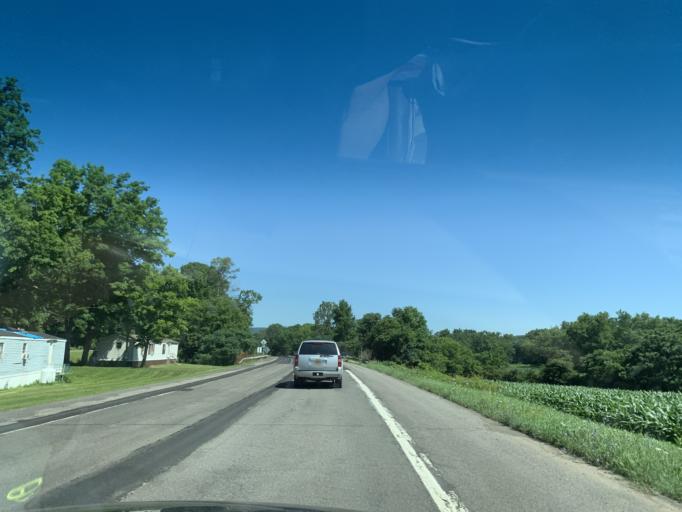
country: US
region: New York
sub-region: Delaware County
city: Sidney
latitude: 42.3593
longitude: -75.4015
